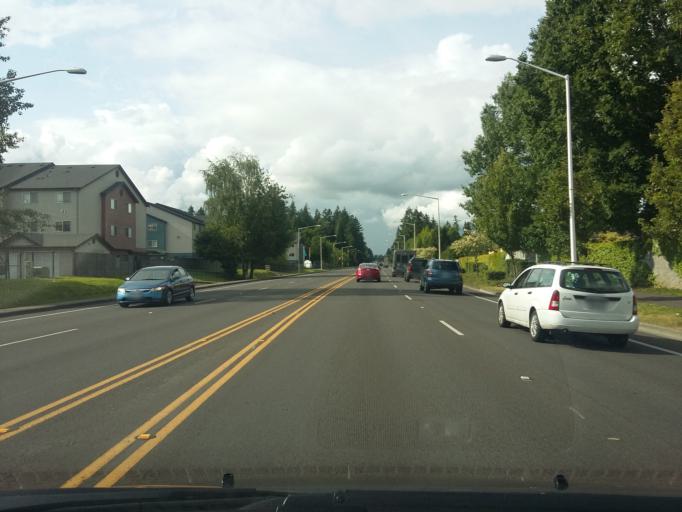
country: US
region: Washington
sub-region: Clark County
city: Walnut Grove
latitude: 45.6529
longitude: -122.6020
